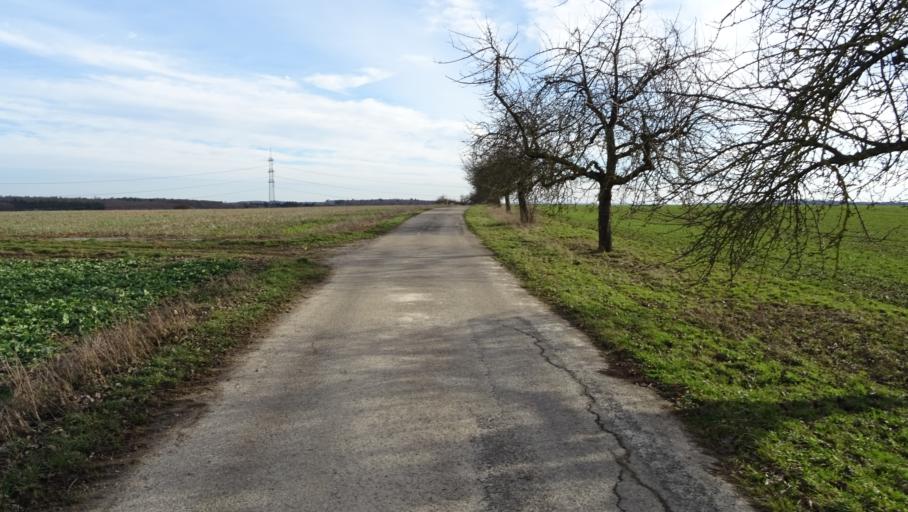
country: DE
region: Baden-Wuerttemberg
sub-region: Karlsruhe Region
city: Billigheim
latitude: 49.3730
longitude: 9.2140
